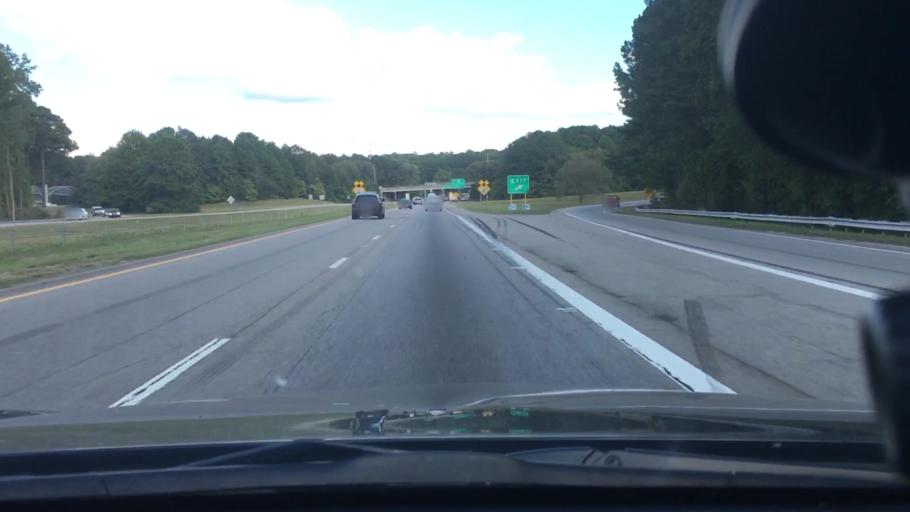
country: US
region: North Carolina
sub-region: Wake County
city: West Raleigh
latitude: 35.8037
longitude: -78.6986
